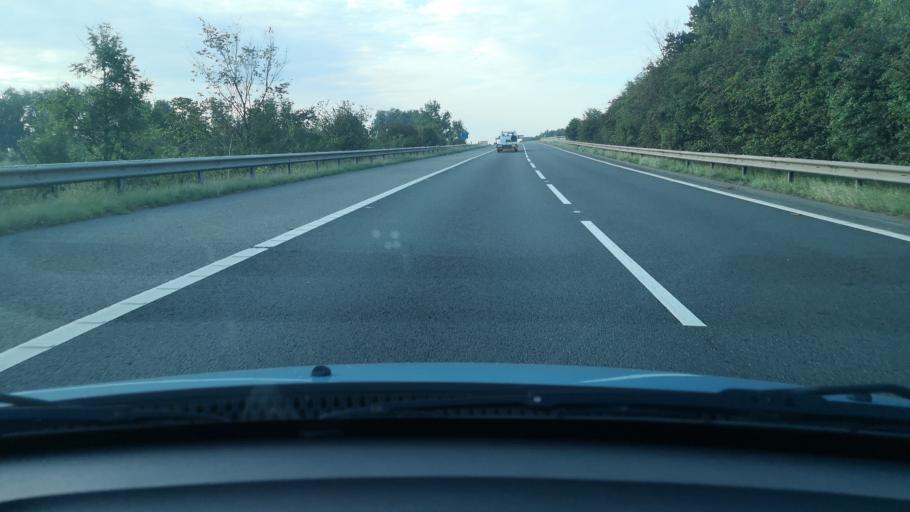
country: GB
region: England
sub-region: East Riding of Yorkshire
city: Rawcliffe
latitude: 53.6797
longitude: -0.9655
